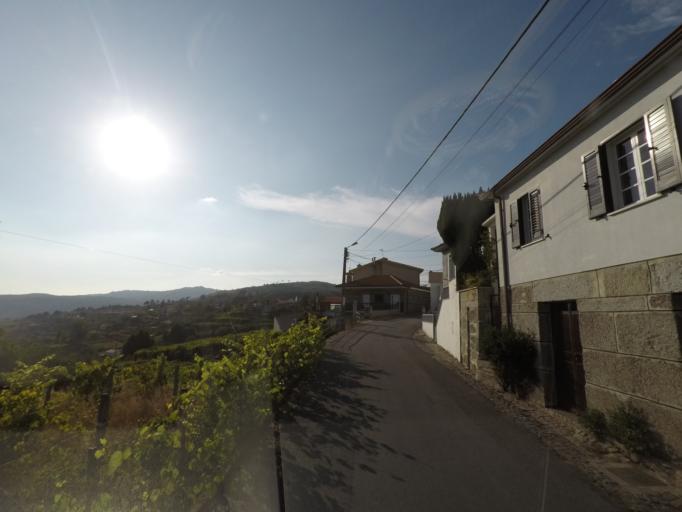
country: PT
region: Vila Real
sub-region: Mesao Frio
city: Mesao Frio
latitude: 41.1660
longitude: -7.9246
